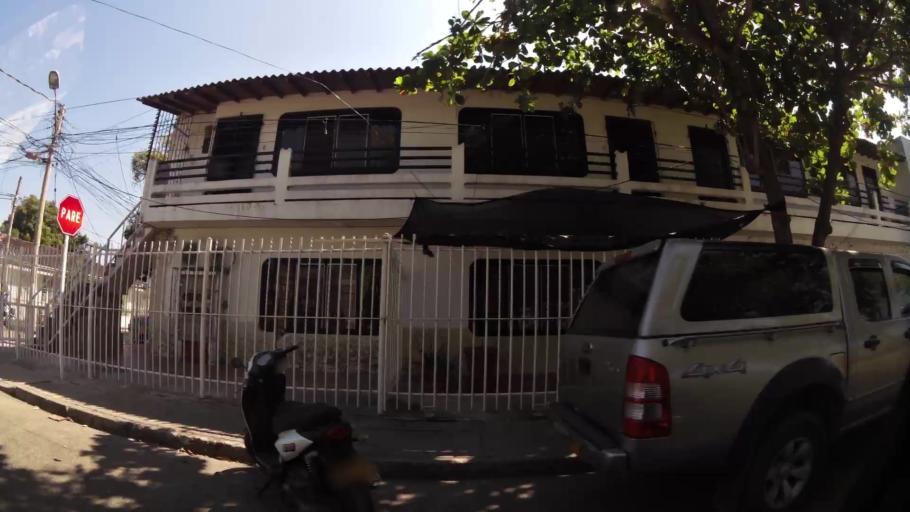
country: CO
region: Bolivar
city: Cartagena
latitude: 10.4410
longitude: -75.5195
